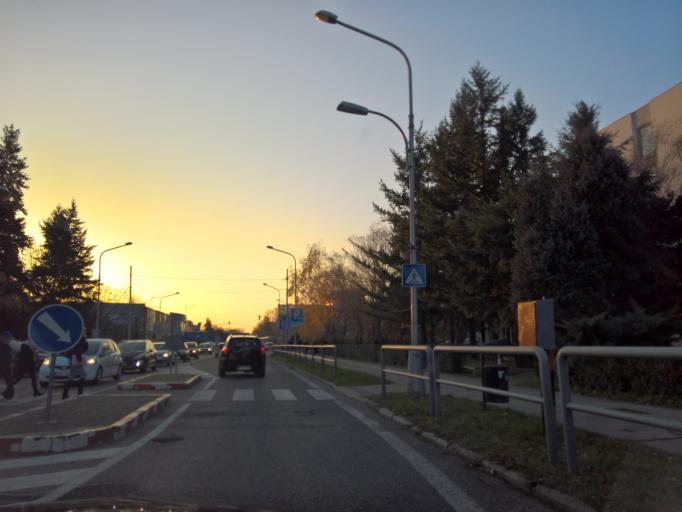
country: SK
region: Nitriansky
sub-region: Okres Nitra
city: Nitra
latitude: 48.3105
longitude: 18.0957
